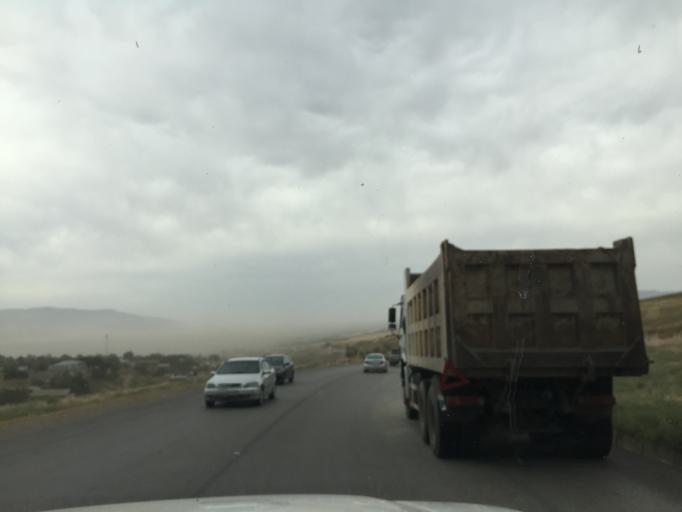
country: TJ
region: Khatlon
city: Danghara
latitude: 38.1597
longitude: 69.2918
